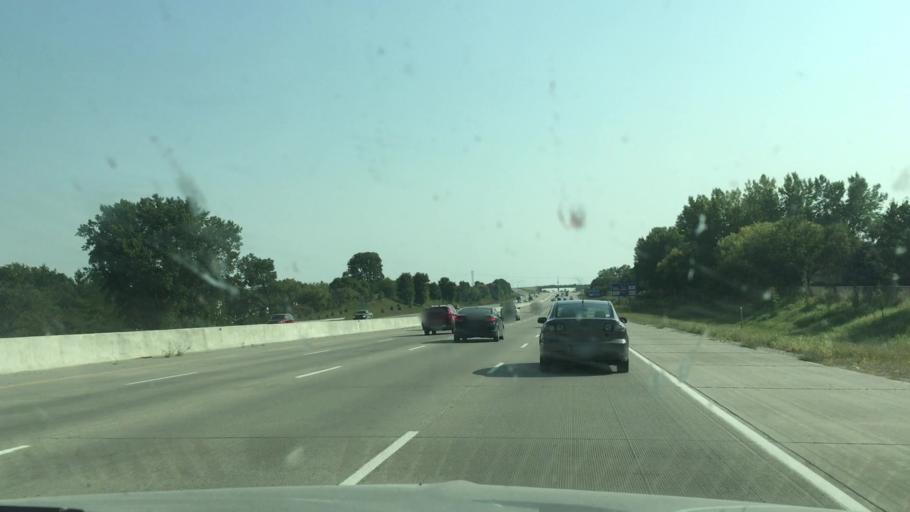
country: US
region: Iowa
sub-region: Polk County
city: Clive
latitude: 41.5715
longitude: -93.7774
